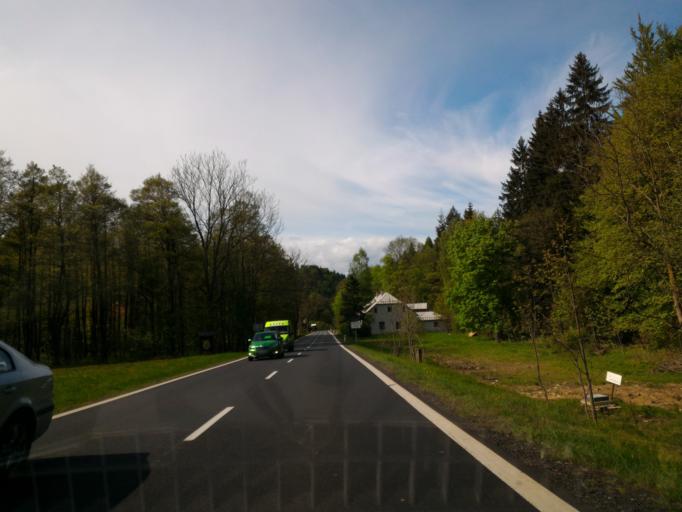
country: CZ
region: Ustecky
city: Dolni Podluzi
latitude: 50.8603
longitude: 14.5888
